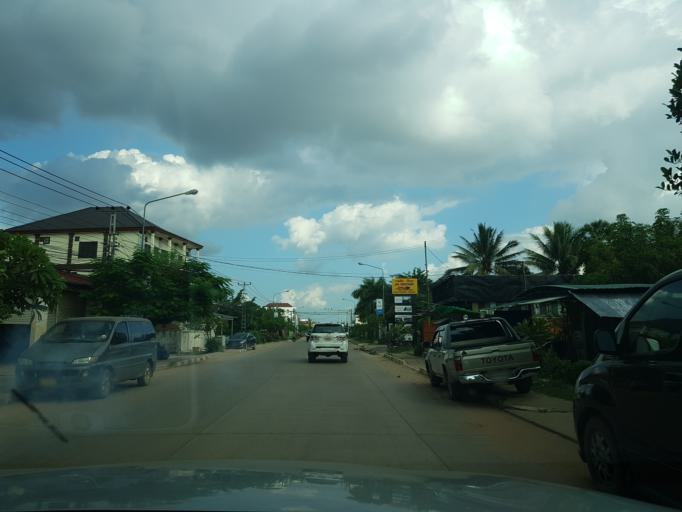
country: TH
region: Nong Khai
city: Si Chiang Mai
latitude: 17.9753
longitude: 102.5468
